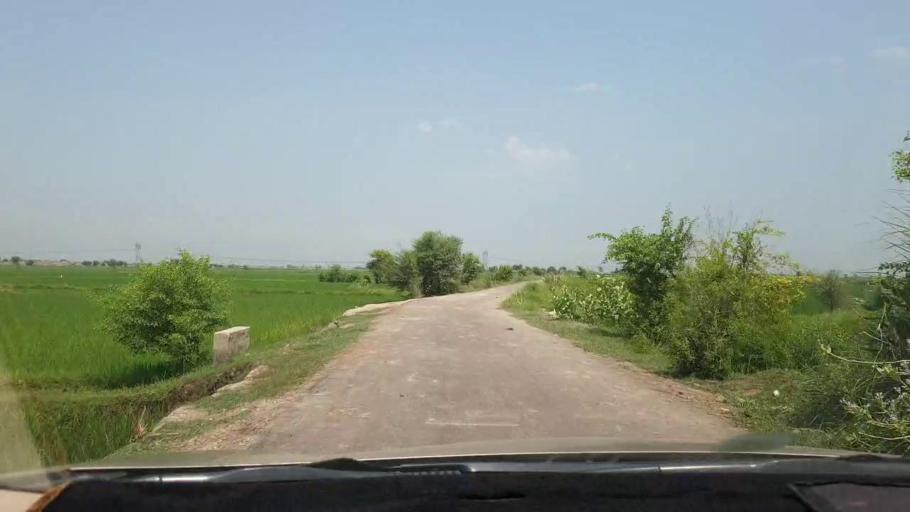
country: PK
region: Sindh
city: Naudero
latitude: 27.6653
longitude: 68.3242
